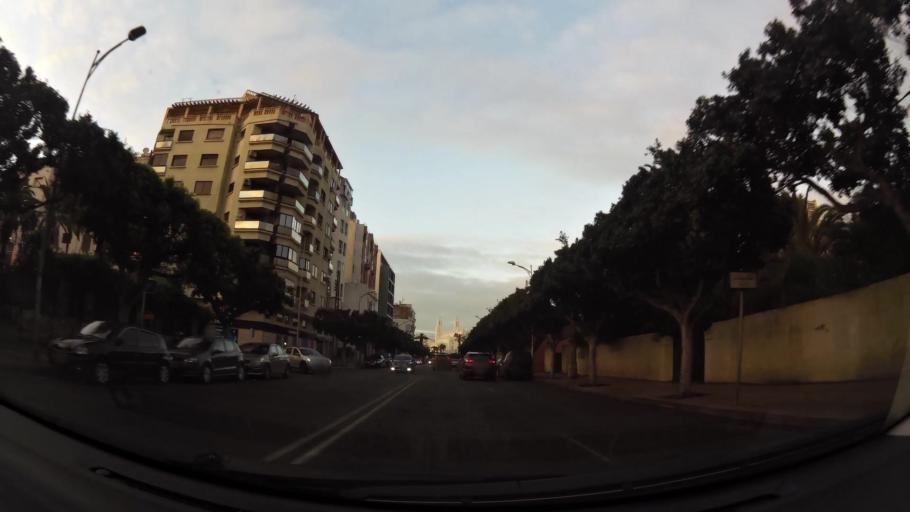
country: MA
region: Grand Casablanca
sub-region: Casablanca
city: Casablanca
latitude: 33.5880
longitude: -7.6273
